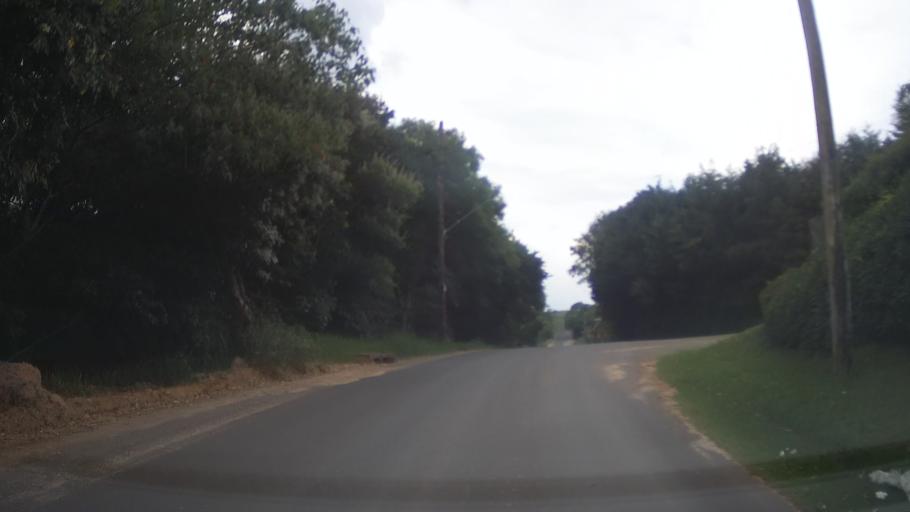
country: BR
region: Sao Paulo
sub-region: Itupeva
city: Itupeva
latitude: -23.1877
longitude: -47.0880
